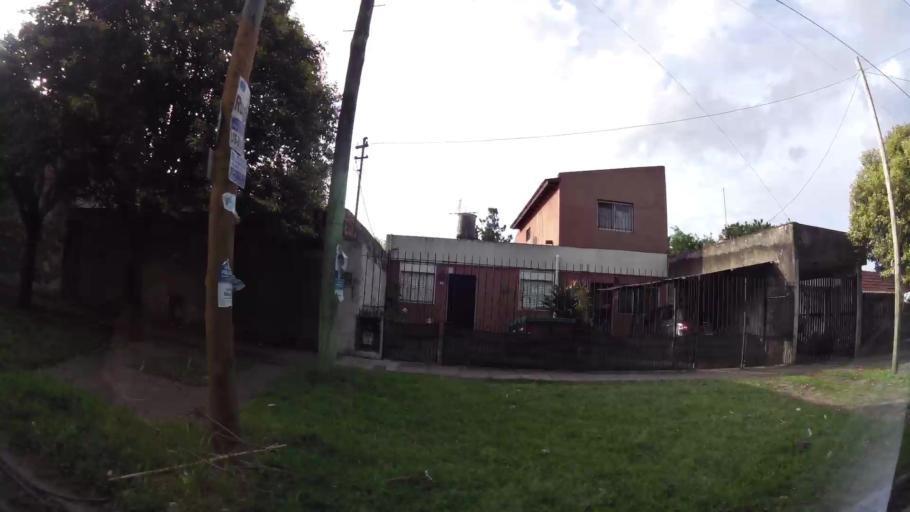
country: AR
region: Buenos Aires
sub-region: Partido de Quilmes
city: Quilmes
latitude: -34.7483
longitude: -58.2543
